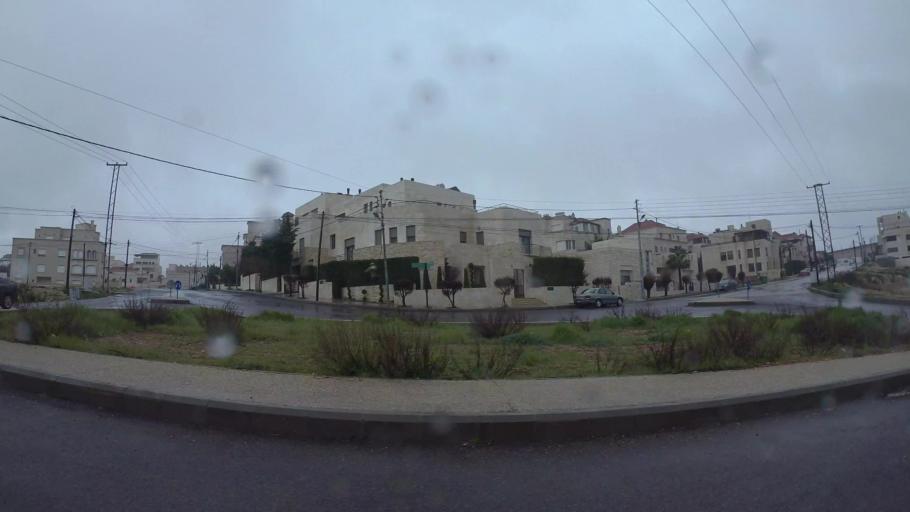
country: JO
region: Amman
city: Al Jubayhah
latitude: 32.0053
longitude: 35.8226
